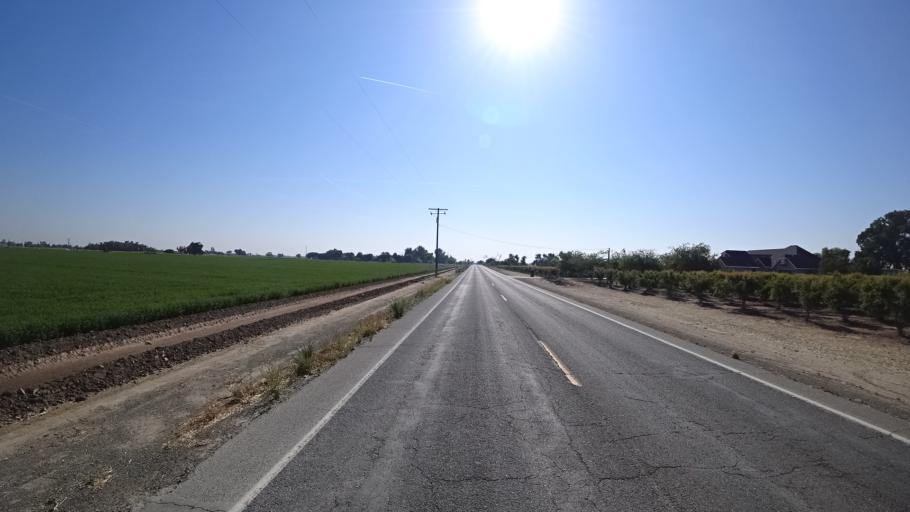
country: US
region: California
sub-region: Fresno County
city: Riverdale
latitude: 36.3439
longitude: -119.8675
